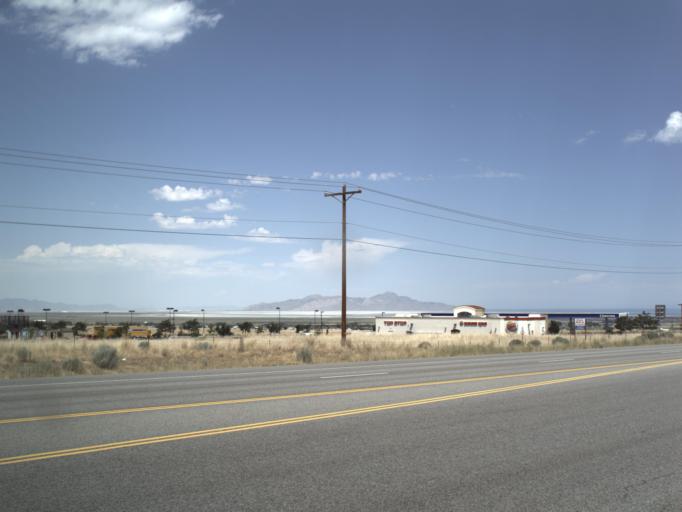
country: US
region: Utah
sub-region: Tooele County
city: Tooele
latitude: 40.5678
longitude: -112.2956
